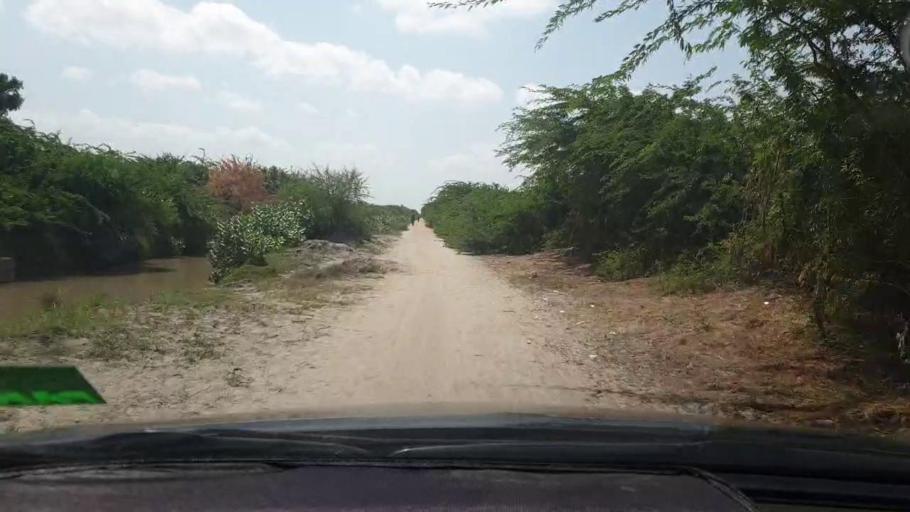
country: PK
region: Sindh
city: Tando Bago
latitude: 24.8736
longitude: 69.0709
